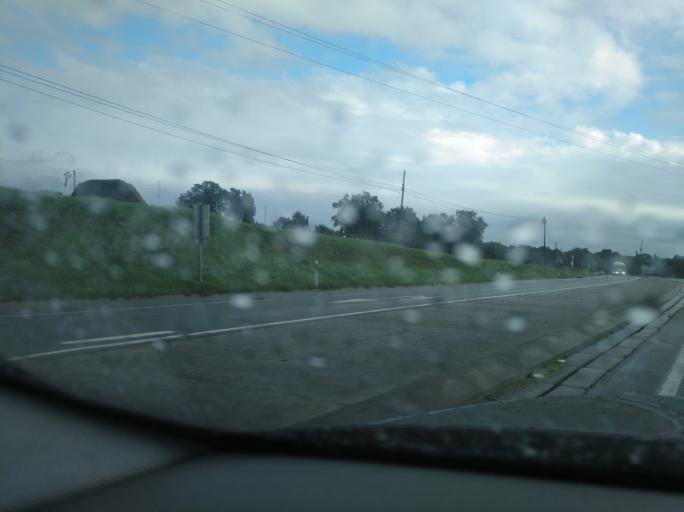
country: PT
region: Setubal
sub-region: Grandola
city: Grandola
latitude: 38.0726
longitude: -8.4162
